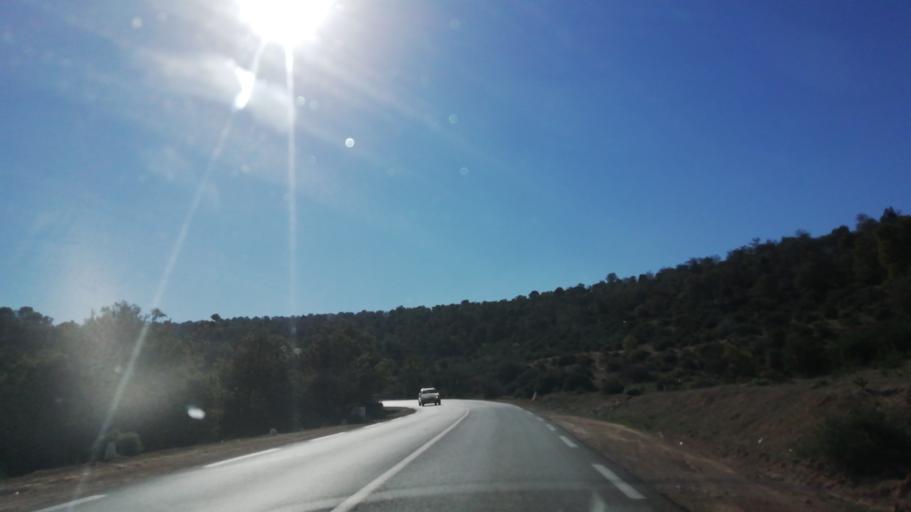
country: DZ
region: Tlemcen
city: Beni Mester
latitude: 34.8189
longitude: -1.6363
